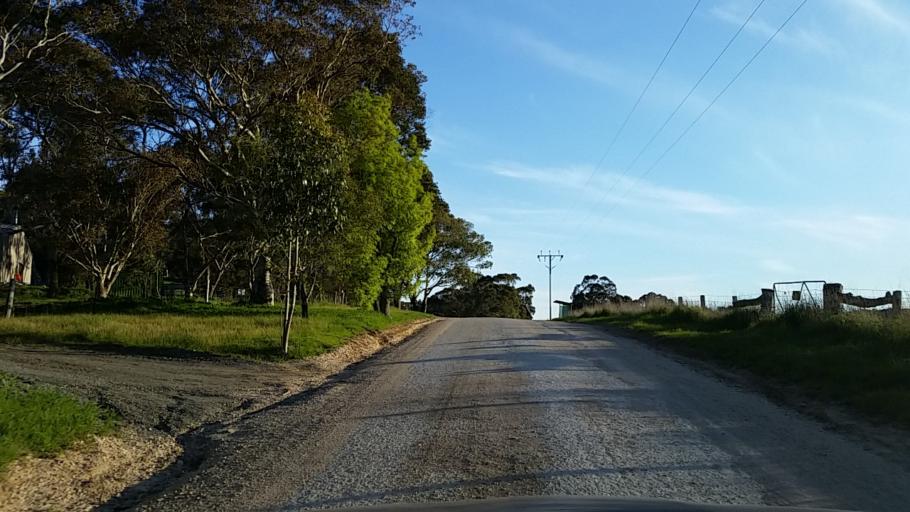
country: AU
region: South Australia
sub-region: Alexandrina
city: Mount Compass
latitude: -35.2914
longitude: 138.6889
